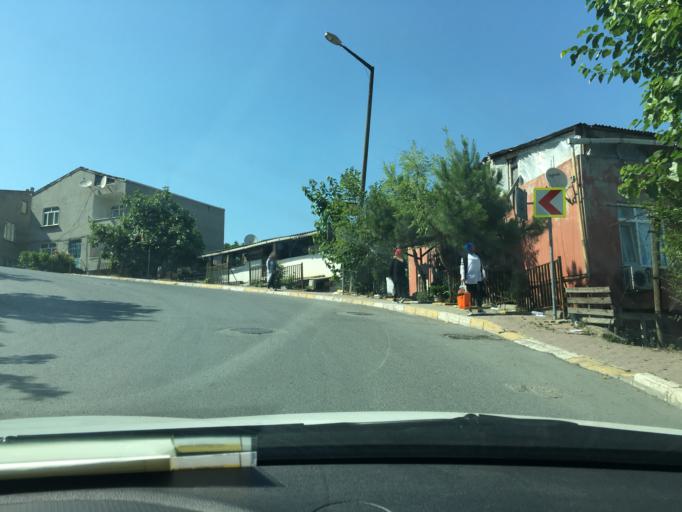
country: TR
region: Istanbul
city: Sisli
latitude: 41.0843
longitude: 28.9458
